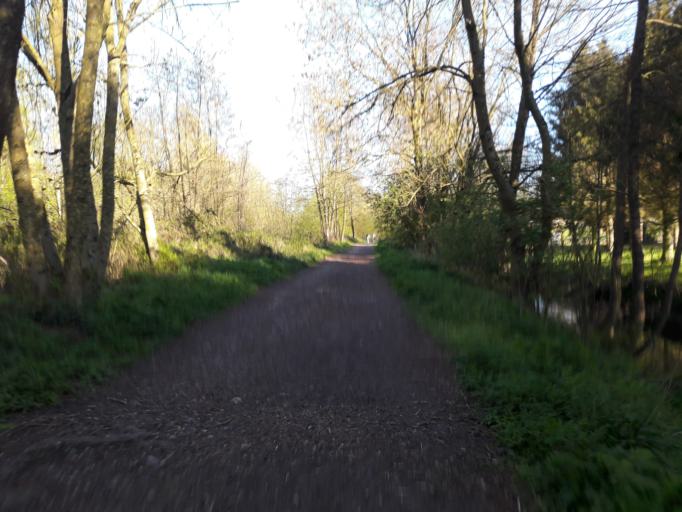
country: FR
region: Nord-Pas-de-Calais
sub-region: Departement du Nord
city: Ferriere-la-Grande
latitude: 50.2543
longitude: 4.0019
